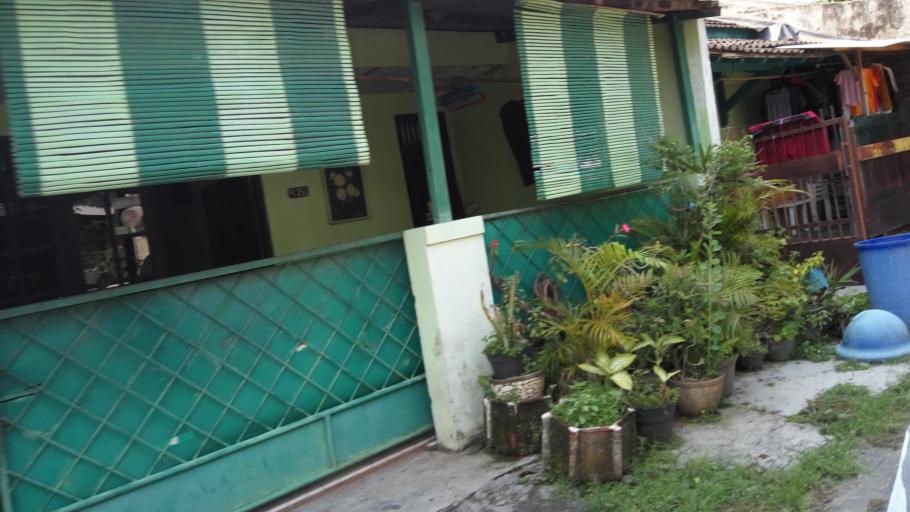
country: ID
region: Central Java
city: Mranggen
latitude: -7.0333
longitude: 110.4740
